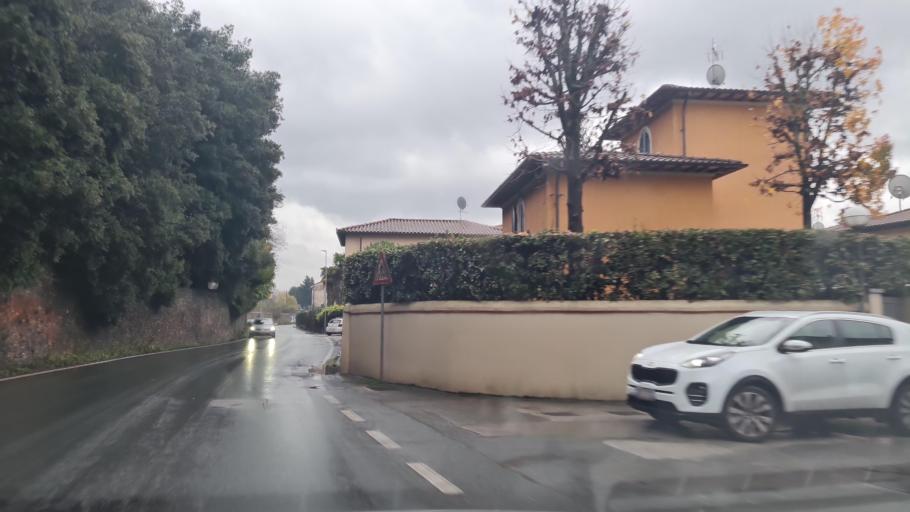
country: IT
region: Tuscany
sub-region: Provincia di Lucca
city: Lucca
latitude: 43.8586
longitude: 10.5009
